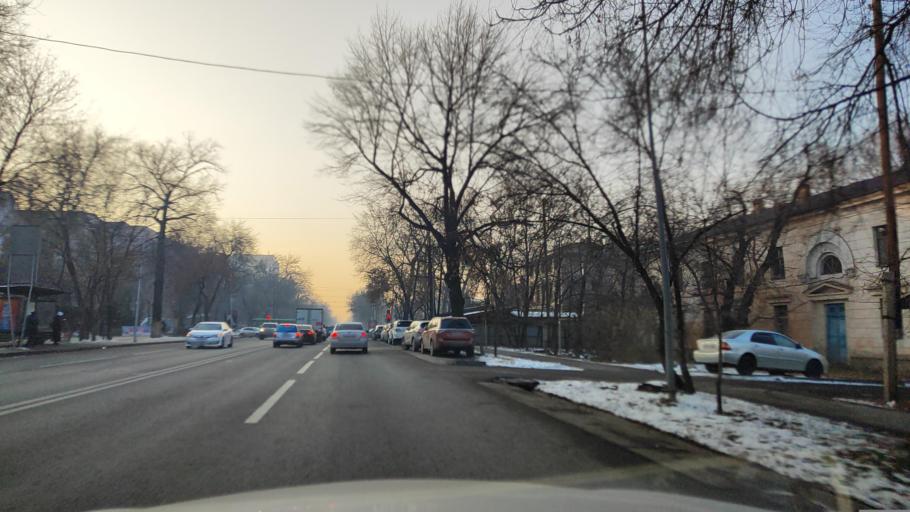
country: KZ
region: Almaty Qalasy
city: Almaty
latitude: 43.2559
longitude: 76.9599
